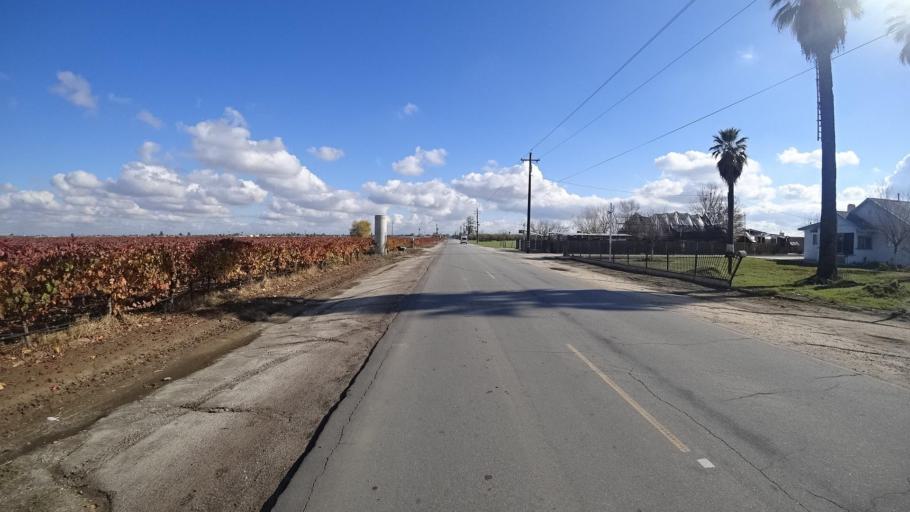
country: US
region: California
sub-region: Kern County
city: McFarland
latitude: 35.6744
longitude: -119.2505
